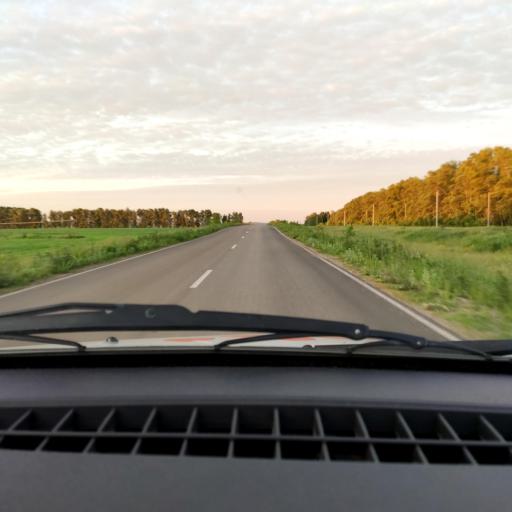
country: RU
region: Bashkortostan
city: Avdon
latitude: 54.5223
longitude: 55.7704
